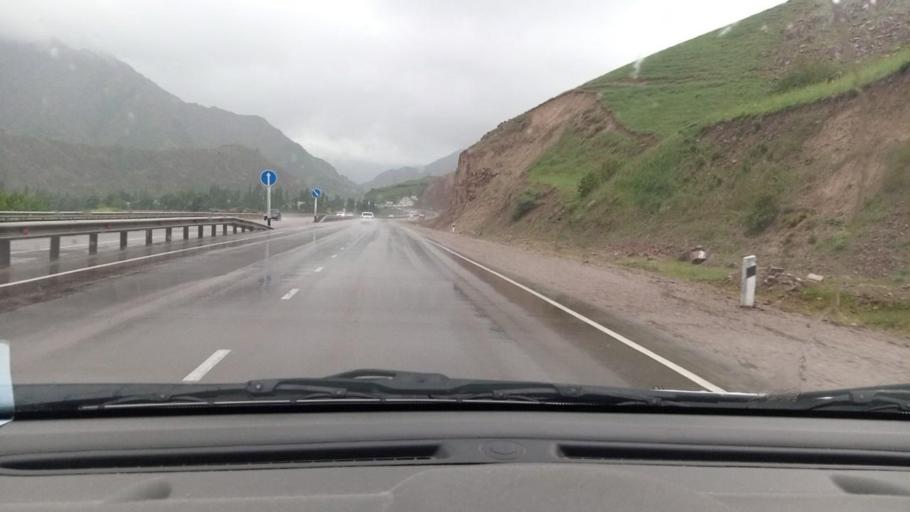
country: UZ
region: Toshkent
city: Angren
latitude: 41.1122
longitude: 70.3384
